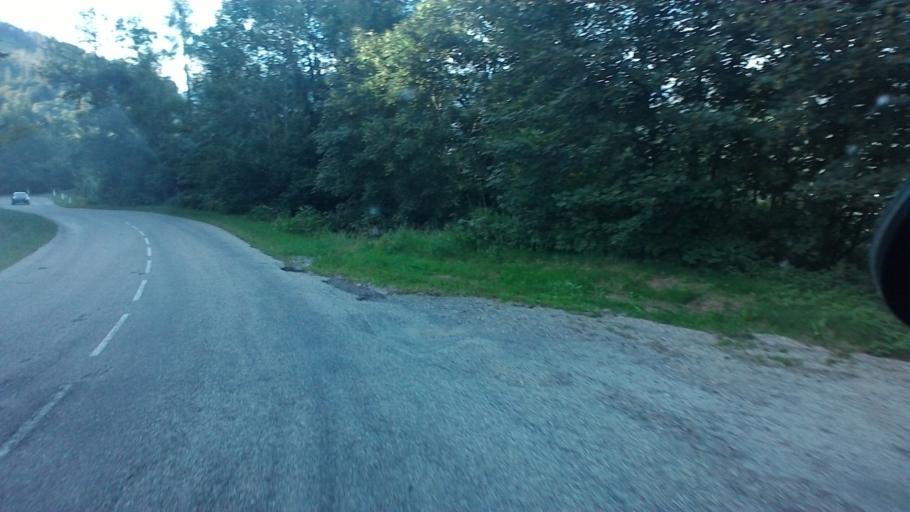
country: FR
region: Lorraine
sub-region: Departement des Vosges
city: Rupt-sur-Moselle
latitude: 47.9047
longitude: 6.6468
